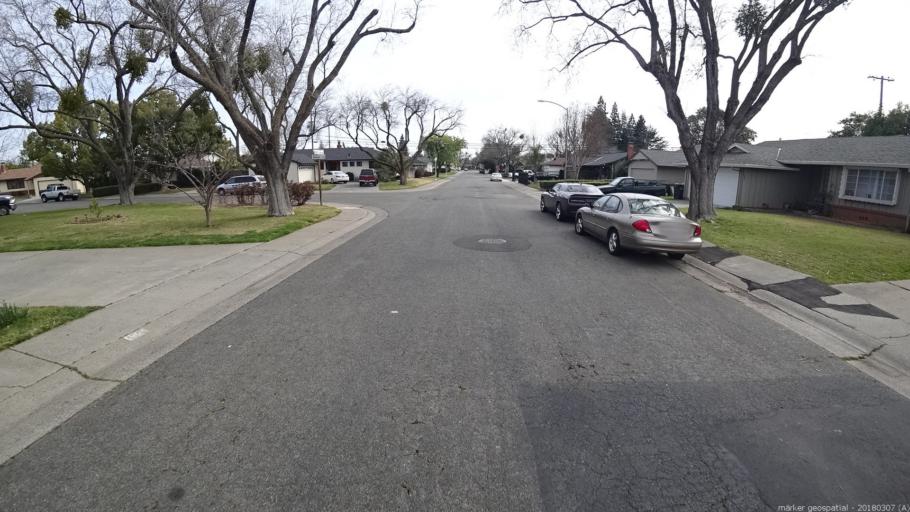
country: US
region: California
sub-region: Sacramento County
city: Parkway
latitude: 38.5260
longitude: -121.4534
